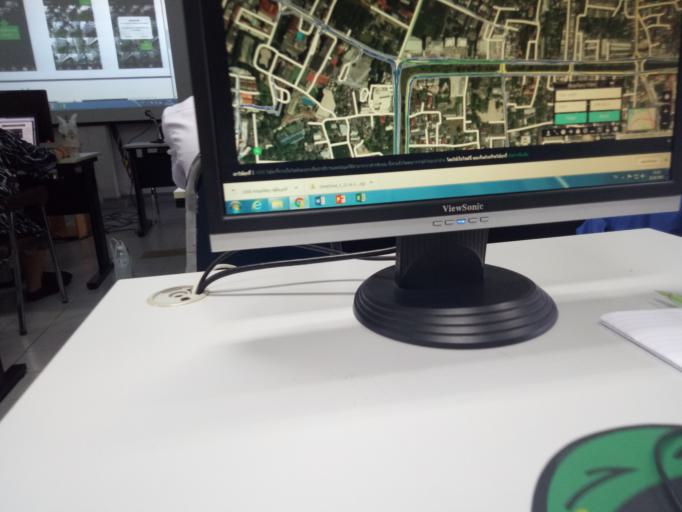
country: TH
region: Chiang Rai
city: Chiang Rai
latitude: 19.9808
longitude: 99.8491
